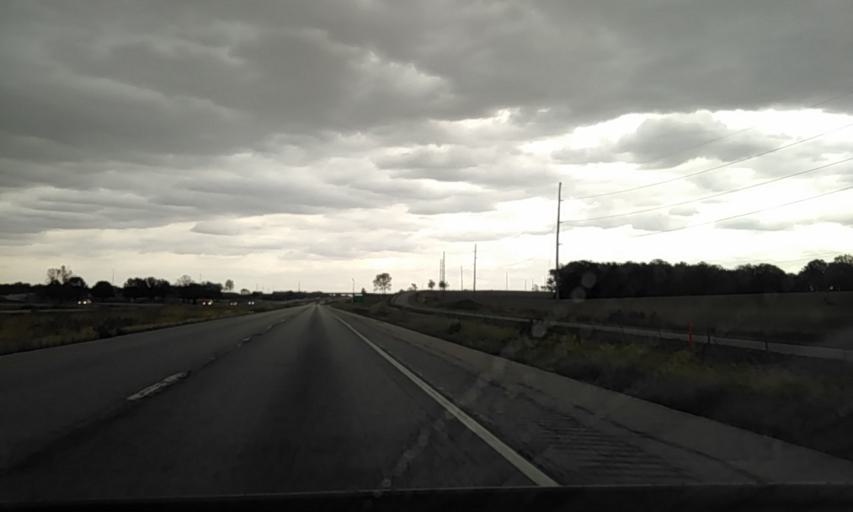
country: US
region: Illinois
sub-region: Bond County
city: Greenville
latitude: 38.8507
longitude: -89.4606
